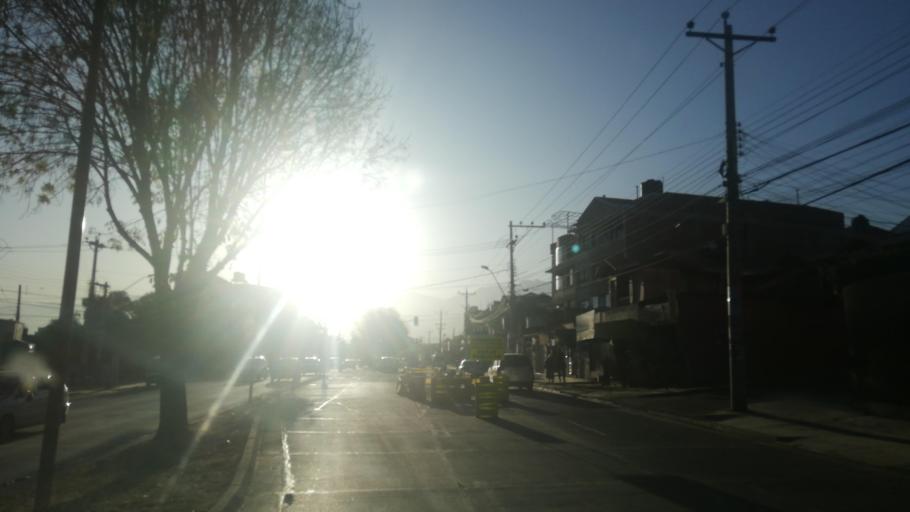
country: BO
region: Cochabamba
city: Cochabamba
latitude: -17.3557
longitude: -66.1766
